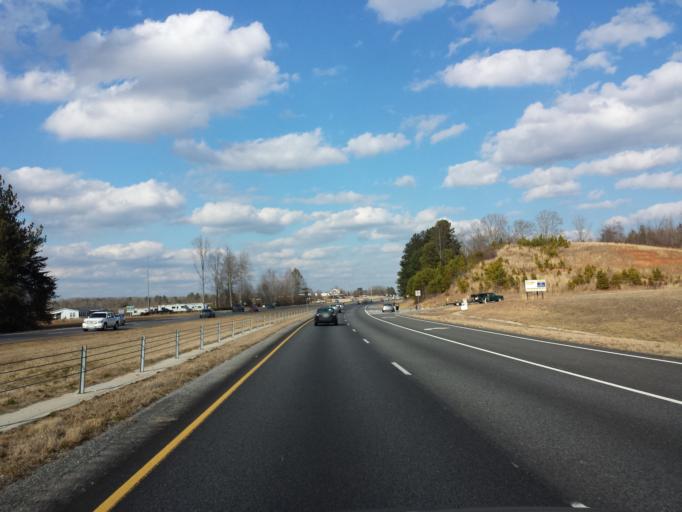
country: US
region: Georgia
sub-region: Dawson County
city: Dawsonville
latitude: 34.3396
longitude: -84.0546
